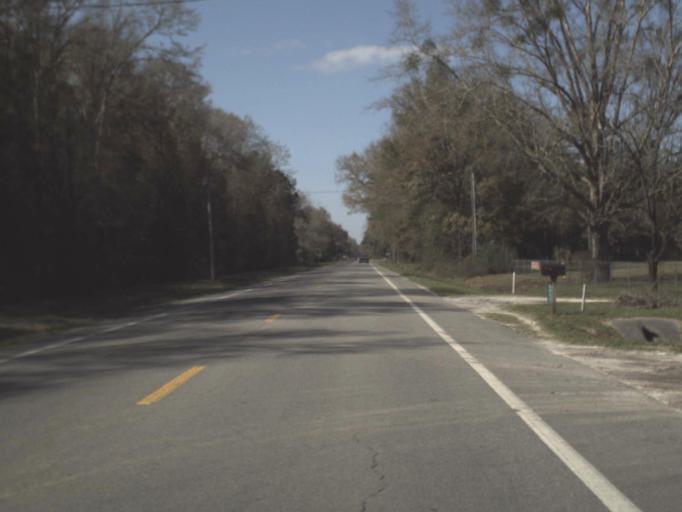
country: US
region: Florida
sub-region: Gulf County
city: Wewahitchka
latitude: 30.0531
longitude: -85.1882
